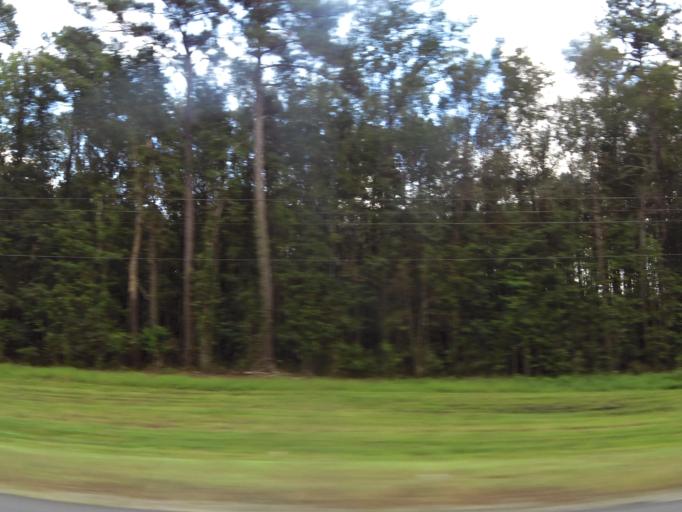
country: US
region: Georgia
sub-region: Liberty County
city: Midway
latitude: 31.8275
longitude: -81.4288
